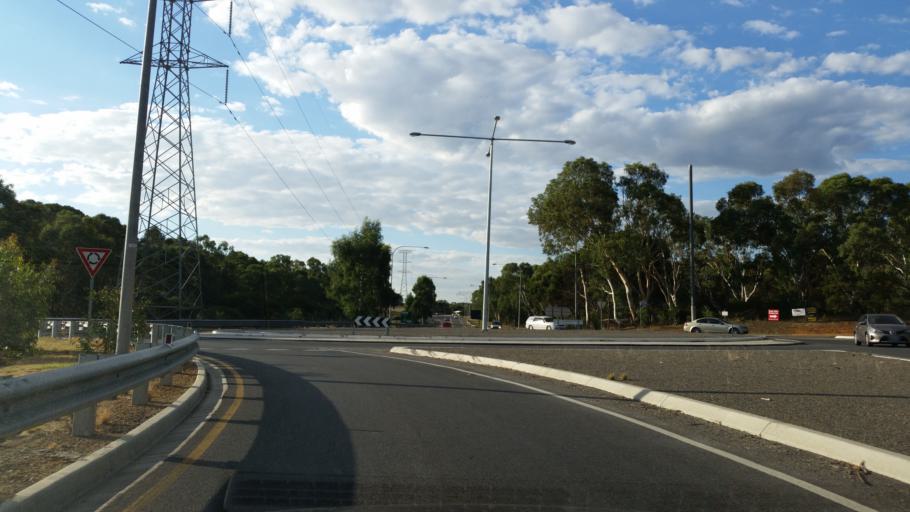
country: AU
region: South Australia
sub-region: Onkaparinga
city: Craigburn Farm
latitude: -35.0743
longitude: 138.5834
